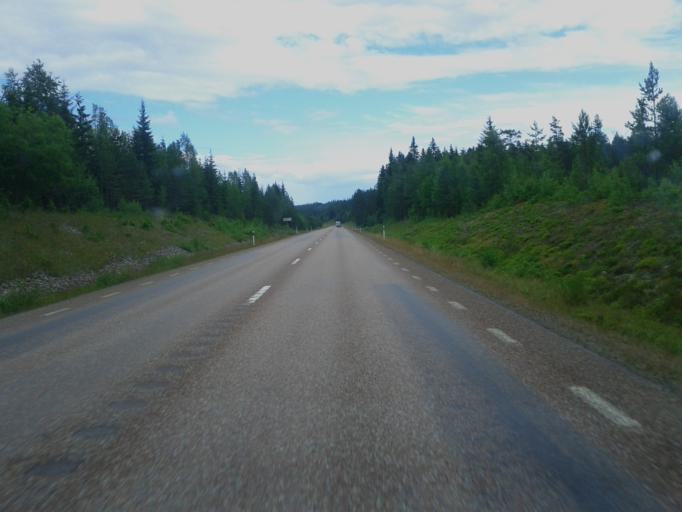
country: SE
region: Dalarna
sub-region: Faluns Kommun
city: Bjursas
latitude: 60.7552
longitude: 15.3417
